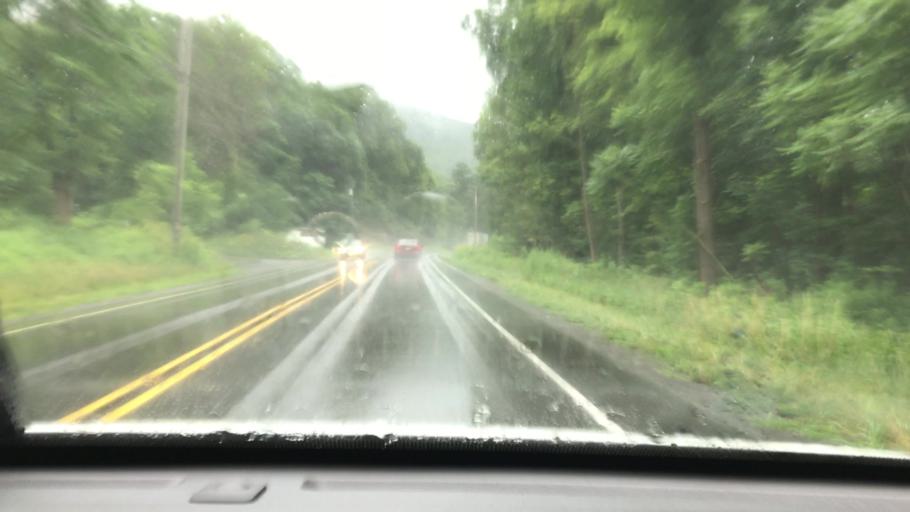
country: US
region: Pennsylvania
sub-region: Blair County
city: Tyrone
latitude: 40.7480
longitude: -78.2103
